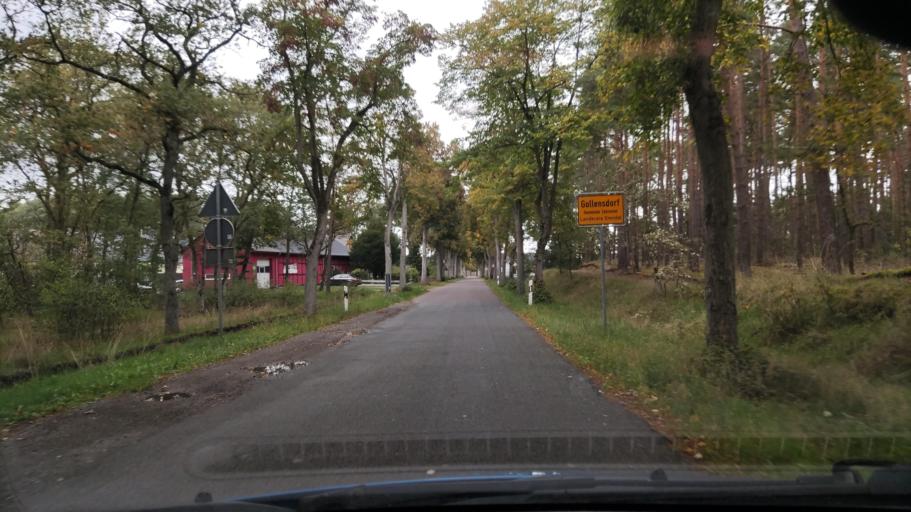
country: DE
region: Saxony-Anhalt
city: Luftkurort Arendsee
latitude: 52.9552
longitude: 11.5465
